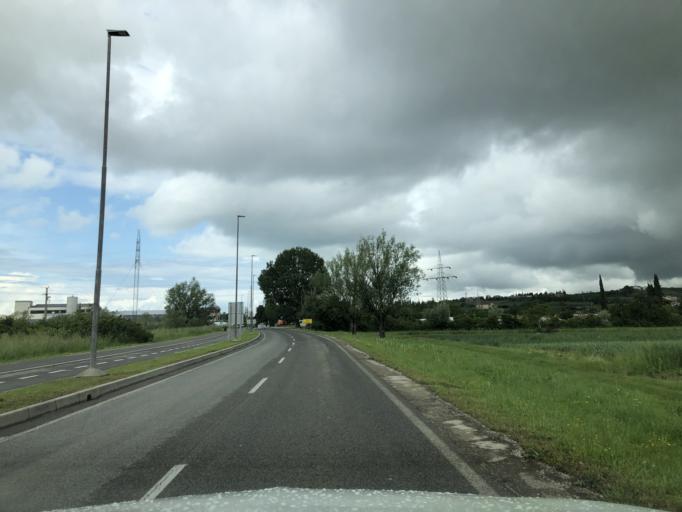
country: SI
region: Koper-Capodistria
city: Koper
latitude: 45.5261
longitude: 13.7406
